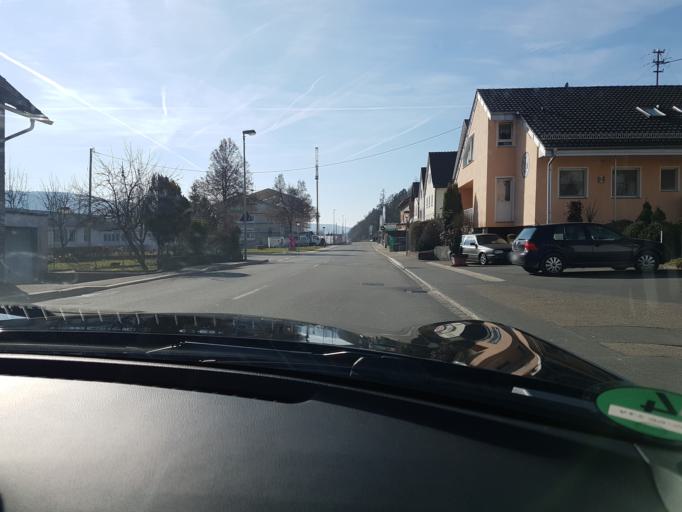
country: DE
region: Baden-Wuerttemberg
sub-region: Regierungsbezirk Stuttgart
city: Krautheim
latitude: 49.3838
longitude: 9.6334
